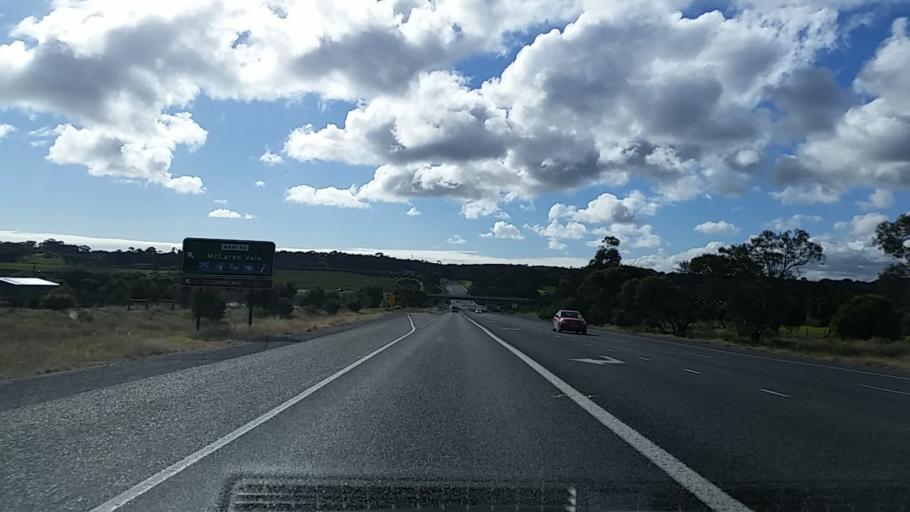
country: AU
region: South Australia
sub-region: Onkaparinga
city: McLaren Vale
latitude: -35.2119
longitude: 138.5235
